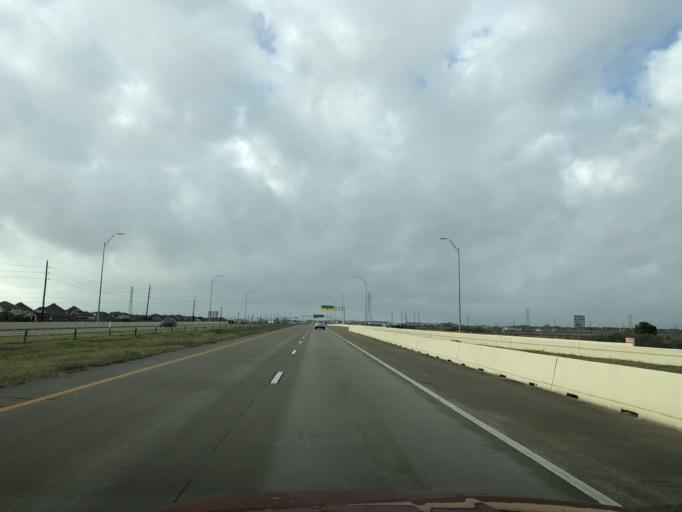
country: US
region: Texas
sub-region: Harris County
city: Katy
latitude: 29.8287
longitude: -95.7628
